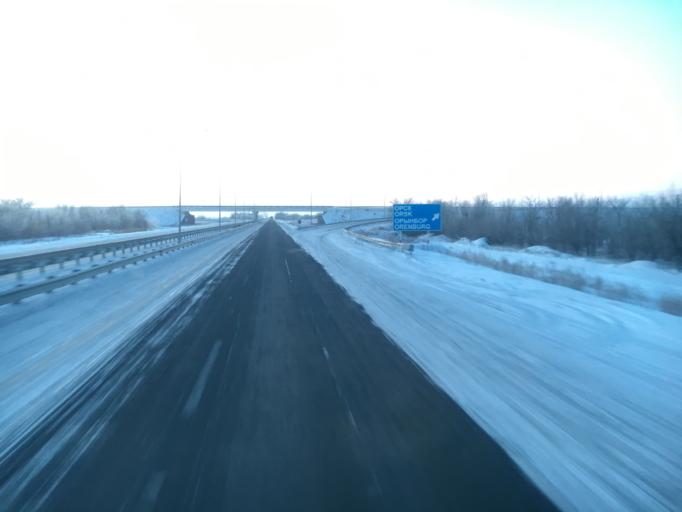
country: KZ
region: Aqtoebe
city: Aqtobe
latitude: 50.2942
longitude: 57.4410
